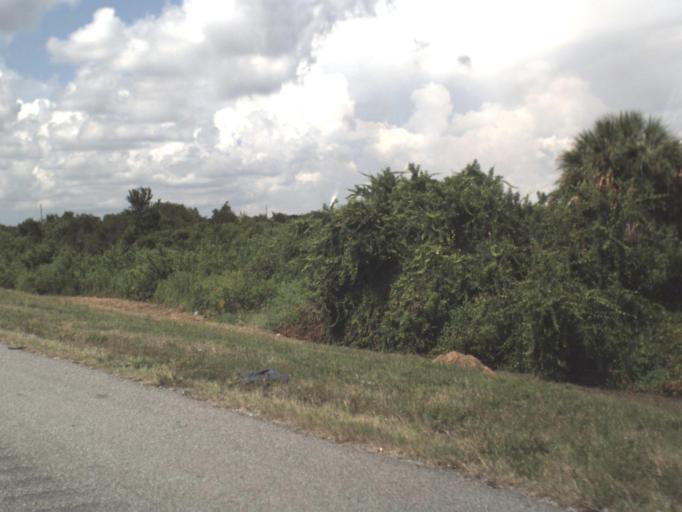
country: US
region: Florida
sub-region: Hillsborough County
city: Riverview
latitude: 27.8389
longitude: -82.3490
